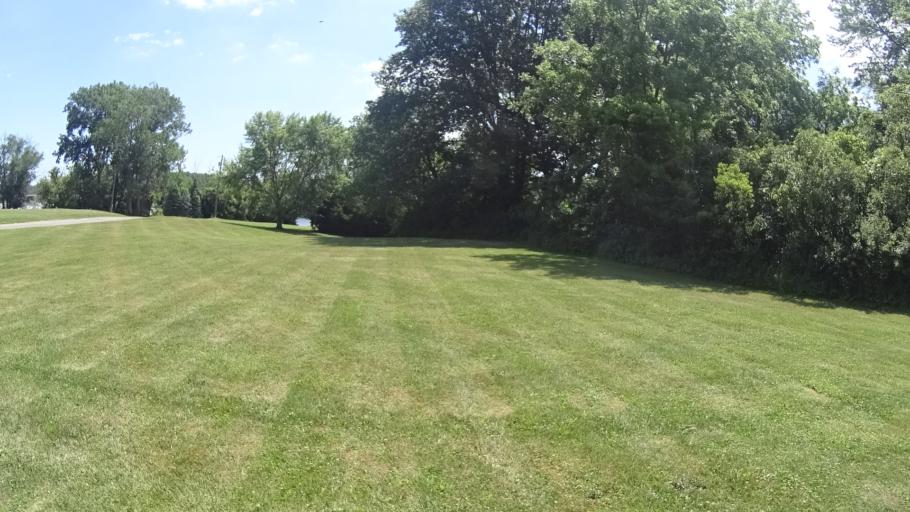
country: US
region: Ohio
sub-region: Erie County
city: Huron
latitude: 41.3860
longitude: -82.5584
